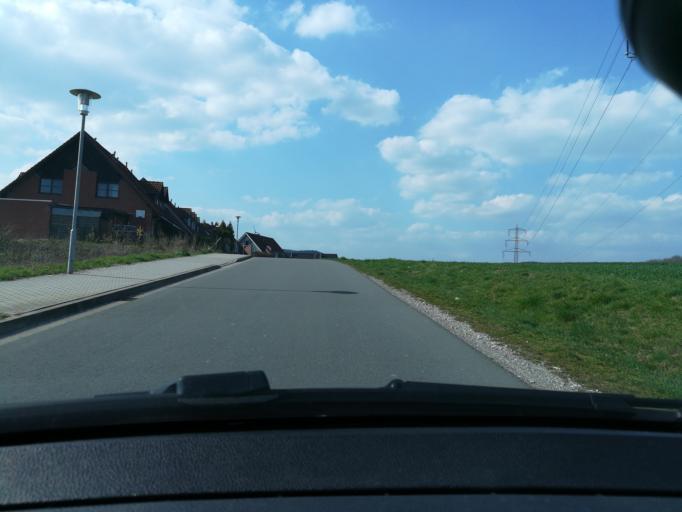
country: DE
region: North Rhine-Westphalia
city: Borgholzhausen
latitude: 52.1020
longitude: 8.3158
